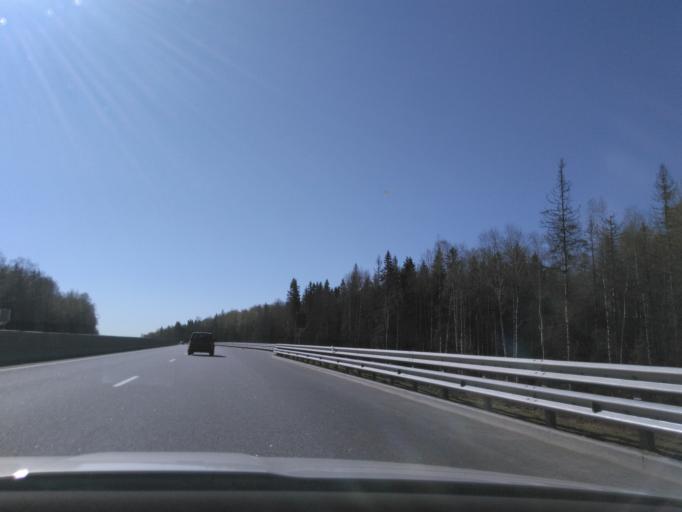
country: RU
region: Moskovskaya
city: Mendeleyevo
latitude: 56.0731
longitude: 37.2168
